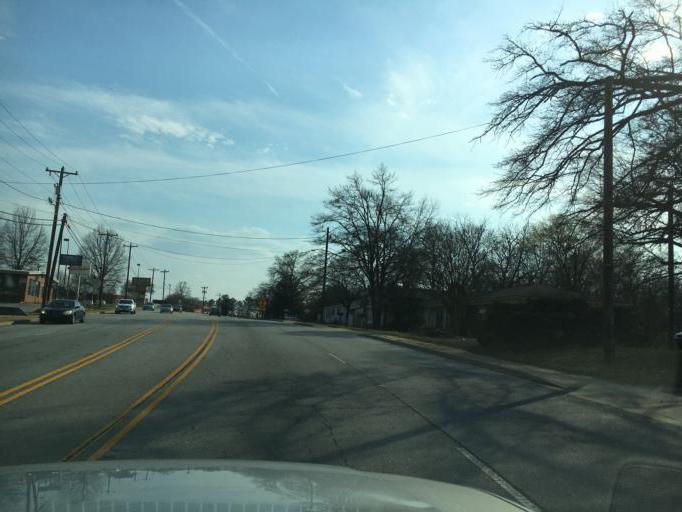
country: US
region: South Carolina
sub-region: Spartanburg County
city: Spartanburg
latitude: 34.9786
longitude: -81.9331
